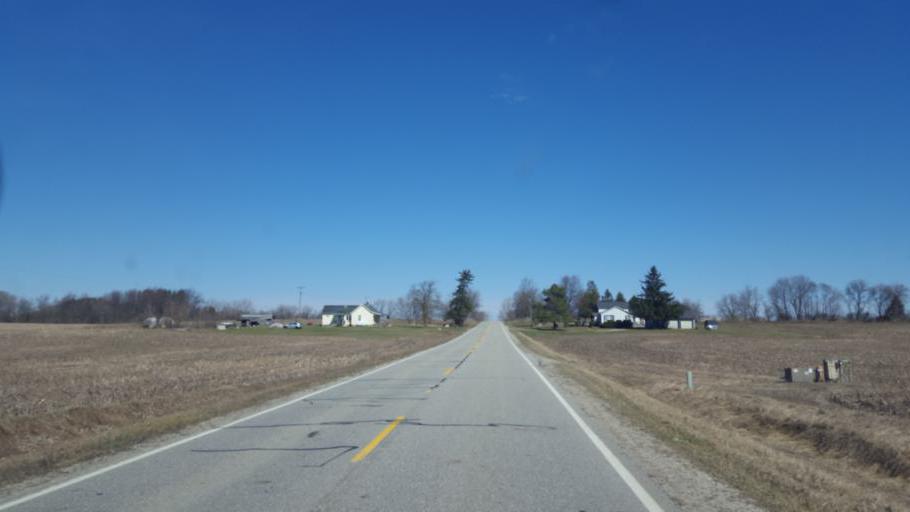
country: US
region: Michigan
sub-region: Montcalm County
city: Edmore
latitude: 43.4693
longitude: -85.0850
